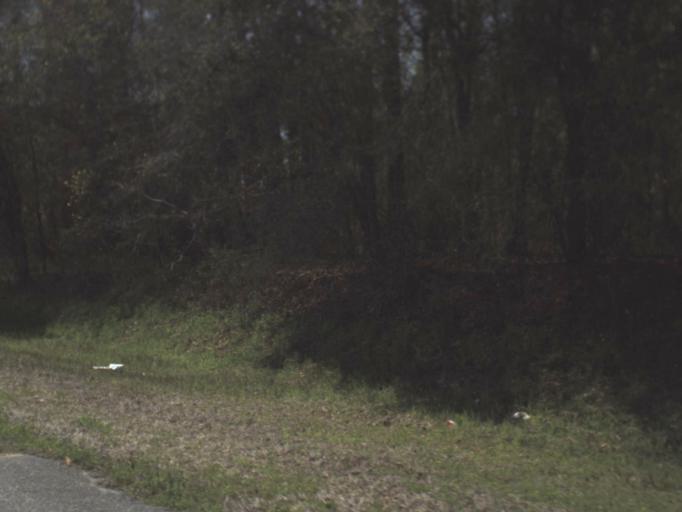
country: US
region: Florida
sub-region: Jefferson County
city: Monticello
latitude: 30.3822
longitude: -84.0067
